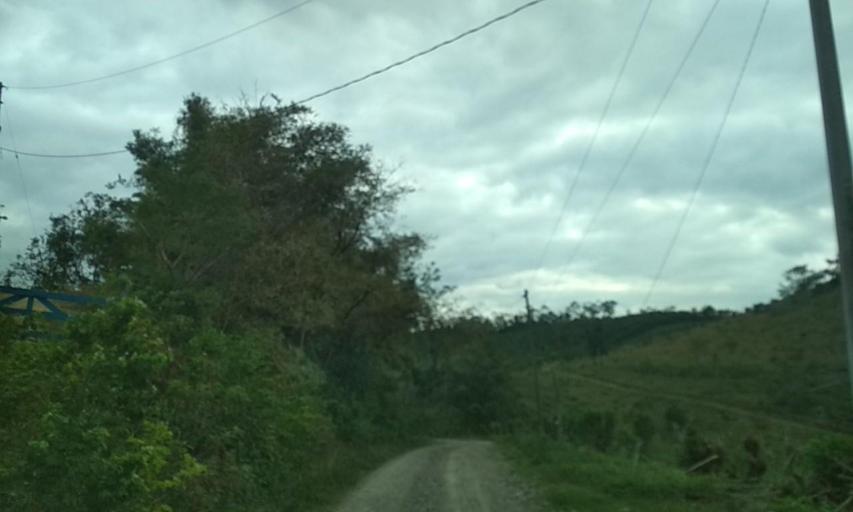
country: MX
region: Veracruz
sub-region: Papantla
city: Polutla
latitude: 20.5073
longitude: -97.3001
